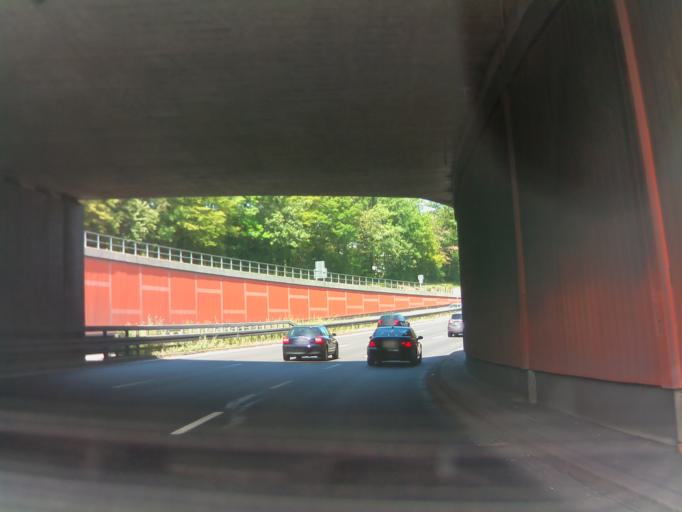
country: DE
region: Baden-Wuerttemberg
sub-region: Regierungsbezirk Stuttgart
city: Gerlingen
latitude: 48.7463
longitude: 9.1130
